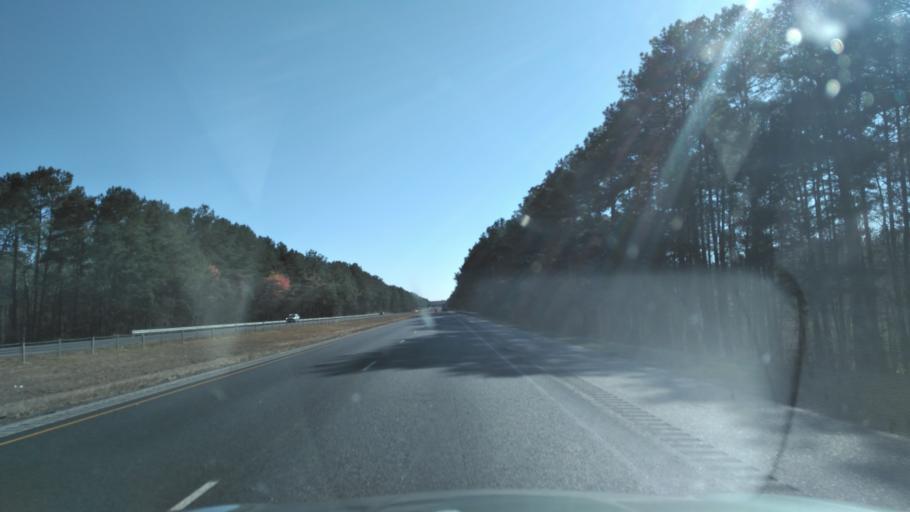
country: US
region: Alabama
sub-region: Butler County
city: Georgiana
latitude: 31.6861
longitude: -86.7508
